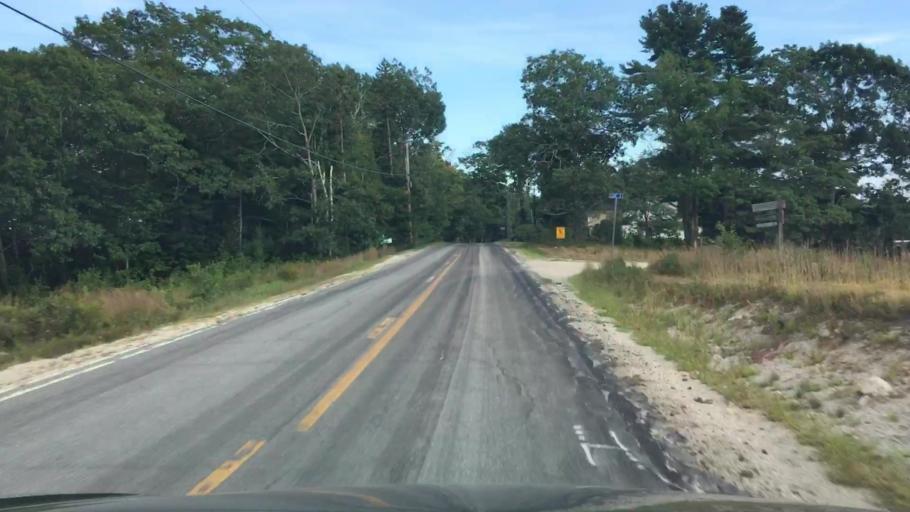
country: US
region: Maine
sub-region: Hancock County
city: Surry
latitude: 44.5132
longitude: -68.6012
